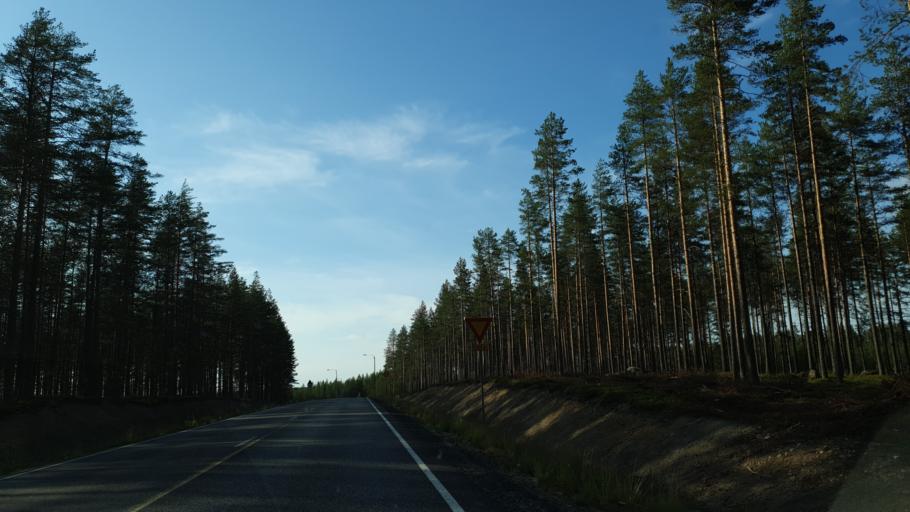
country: FI
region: Kainuu
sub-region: Kehys-Kainuu
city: Kuhmo
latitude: 64.0972
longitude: 29.4761
